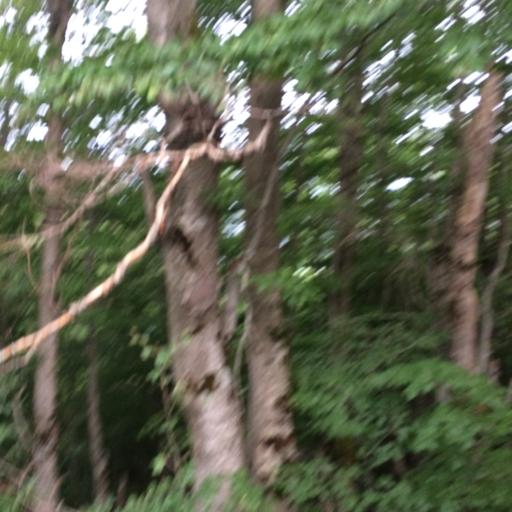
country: AL
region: Shkoder
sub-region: Rrethi i Shkodres
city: Nicaj-Shale
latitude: 42.4002
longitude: 19.7860
